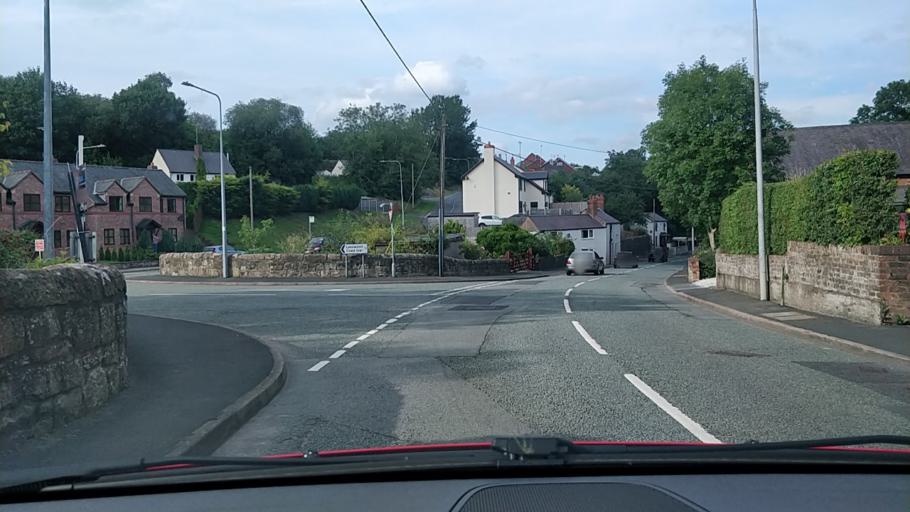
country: GB
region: Wales
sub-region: County of Flintshire
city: Leeswood
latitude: 53.1258
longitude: -3.0904
